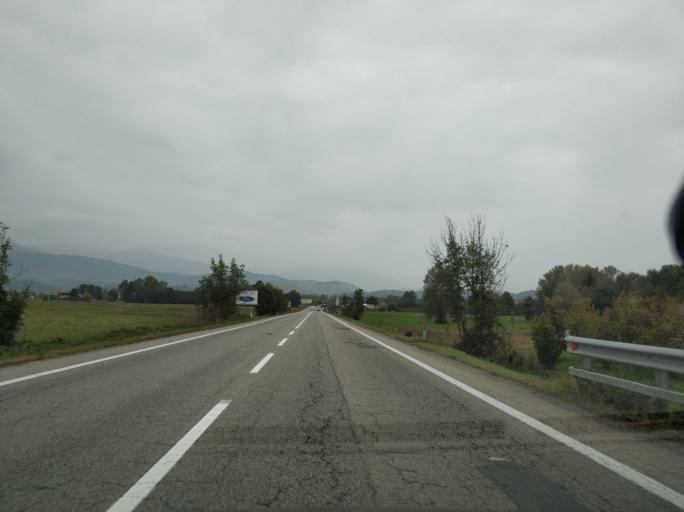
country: IT
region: Piedmont
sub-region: Provincia di Torino
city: Castellamonte
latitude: 45.3765
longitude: 7.7318
